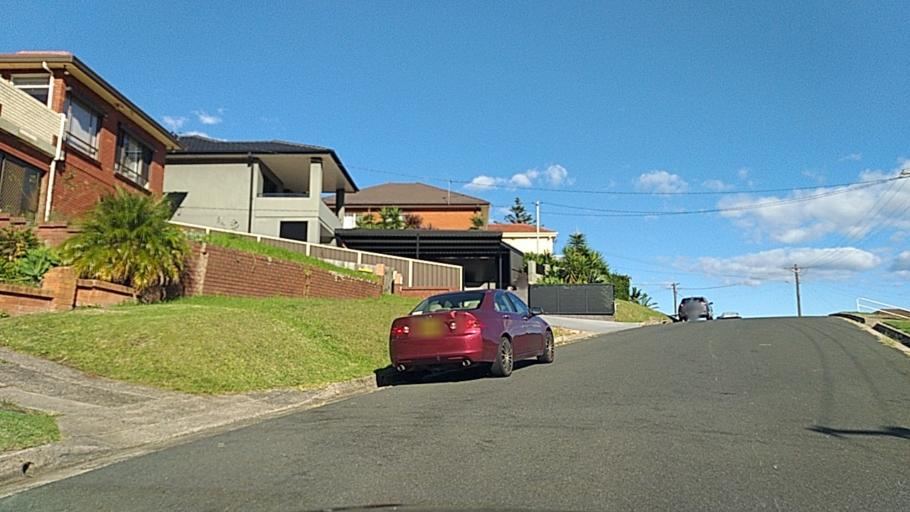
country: AU
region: New South Wales
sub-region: Wollongong
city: Port Kembla
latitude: -34.4831
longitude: 150.8920
